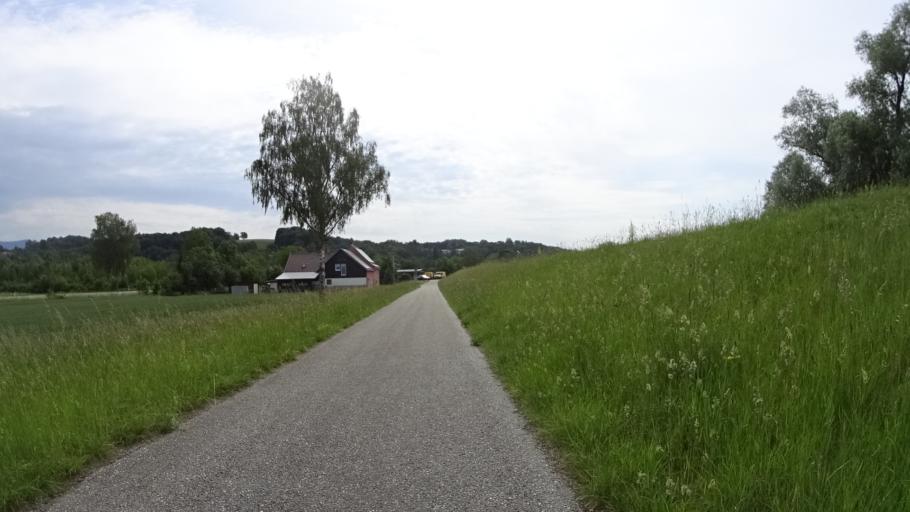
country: DE
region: Bavaria
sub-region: Lower Bavaria
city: Metten
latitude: 48.8463
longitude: 12.9072
